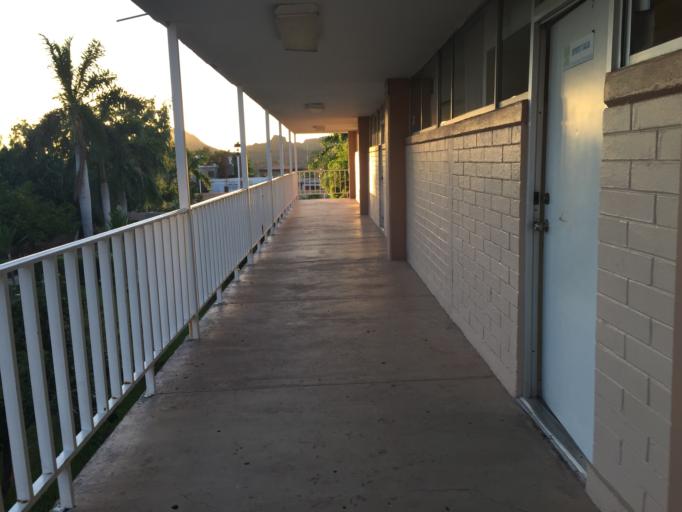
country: MX
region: Sonora
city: Heroica Guaymas
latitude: 27.9690
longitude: -110.9199
